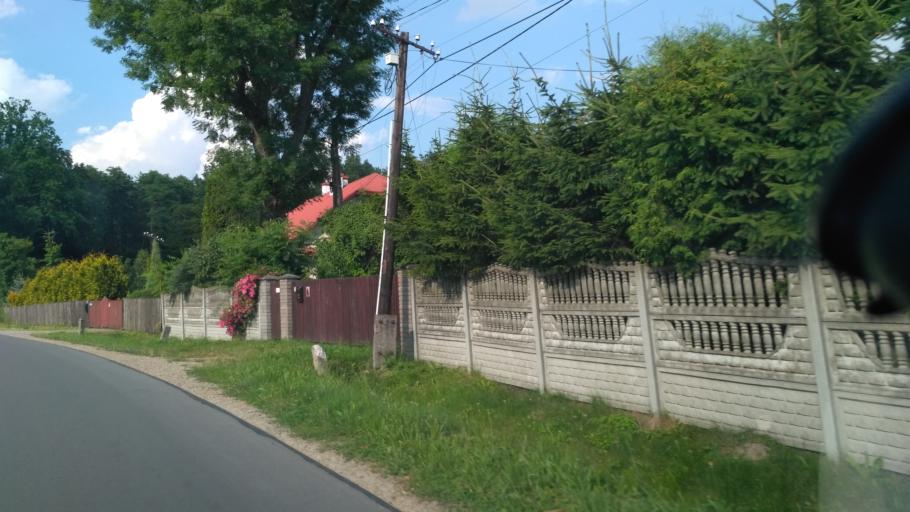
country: PL
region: Subcarpathian Voivodeship
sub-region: Powiat rzeszowski
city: Glogow Malopolski
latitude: 50.1588
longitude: 21.9823
